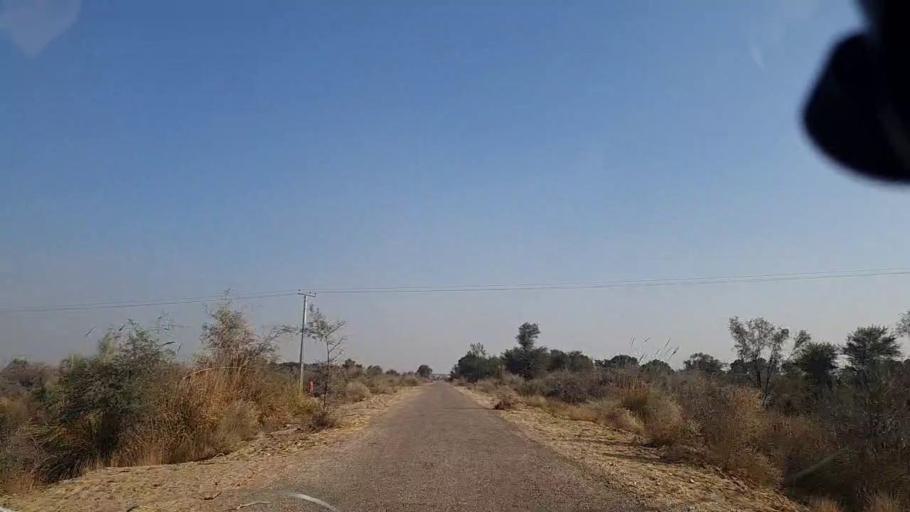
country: PK
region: Sindh
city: Khanpur
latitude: 27.6443
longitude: 69.5979
